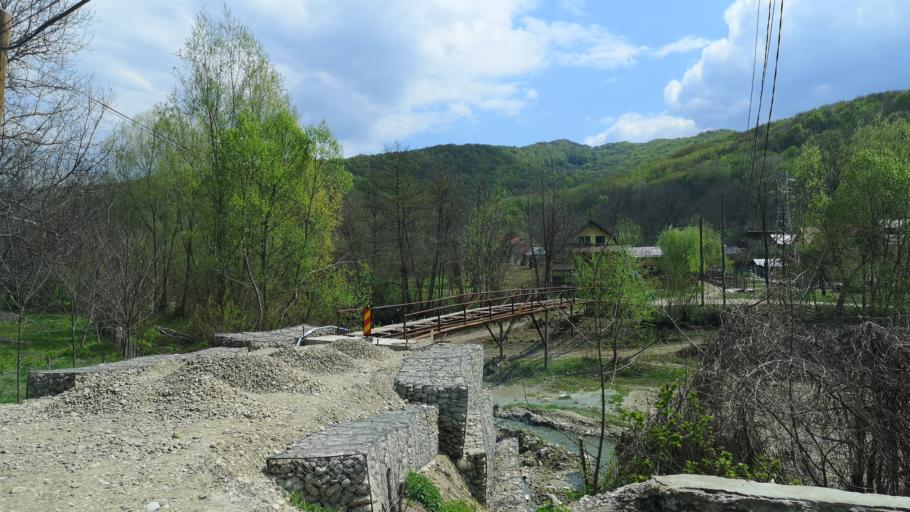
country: RO
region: Prahova
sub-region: Comuna Soimari
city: Soimari
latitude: 45.1631
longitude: 26.2075
